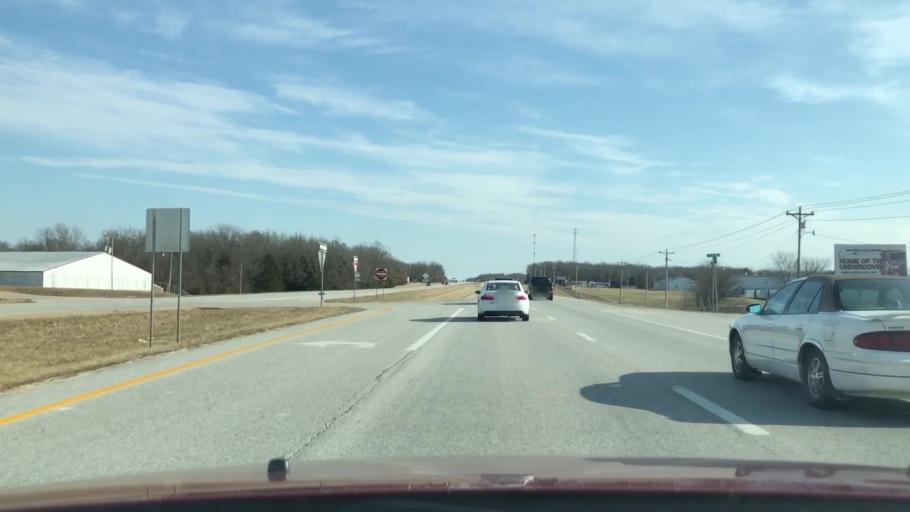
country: US
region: Missouri
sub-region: Webster County
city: Rogersville
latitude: 37.1154
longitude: -93.0298
